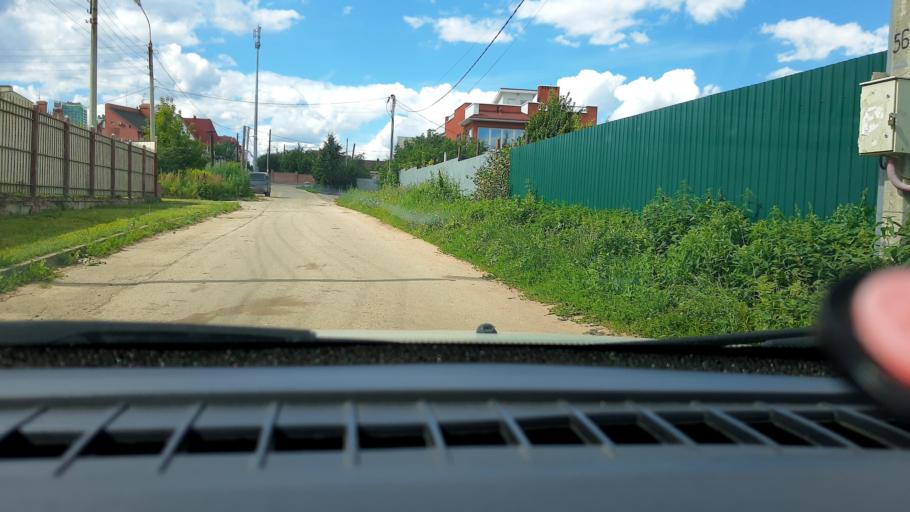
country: RU
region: Nizjnij Novgorod
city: Afonino
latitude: 56.3016
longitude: 44.0917
